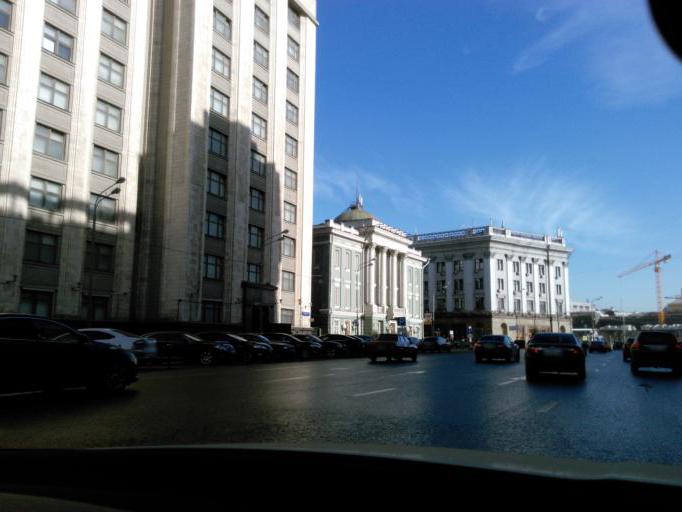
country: RU
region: Moscow
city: Moscow
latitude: 55.7577
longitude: 37.6165
